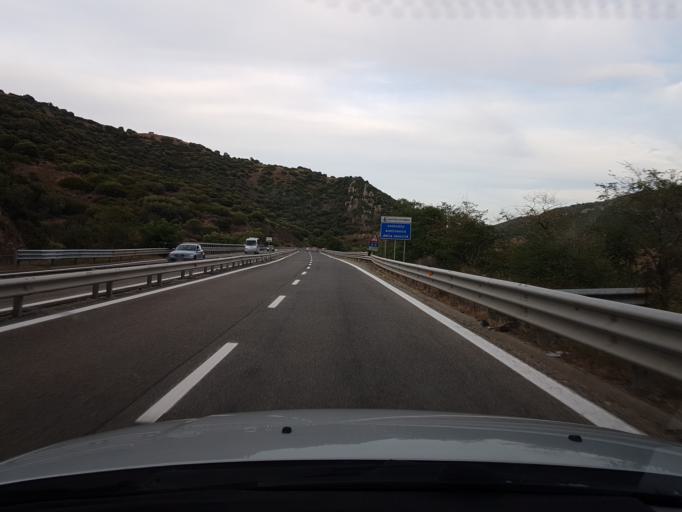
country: IT
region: Sardinia
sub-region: Provincia di Nuoro
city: Nuoro
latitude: 40.3462
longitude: 9.3262
